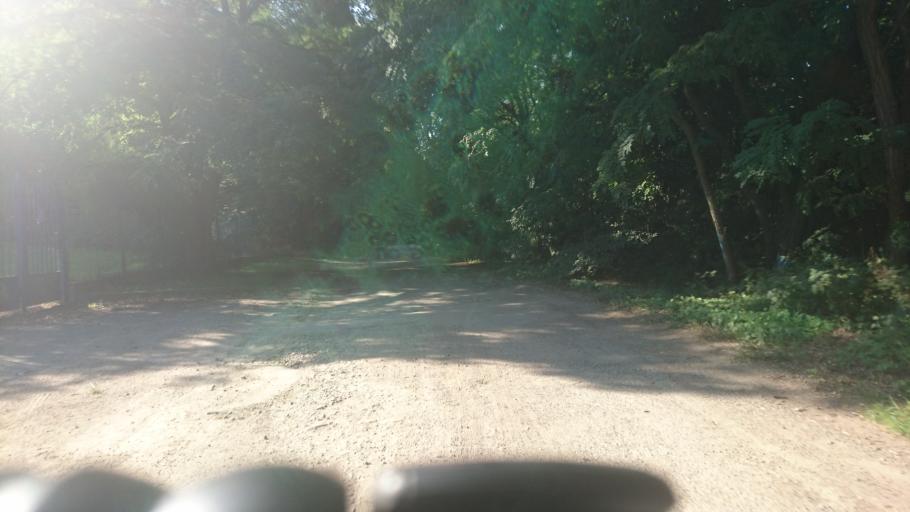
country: CZ
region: South Moravian
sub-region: Mesto Brno
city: Mokra Hora
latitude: 49.2254
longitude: 16.5710
